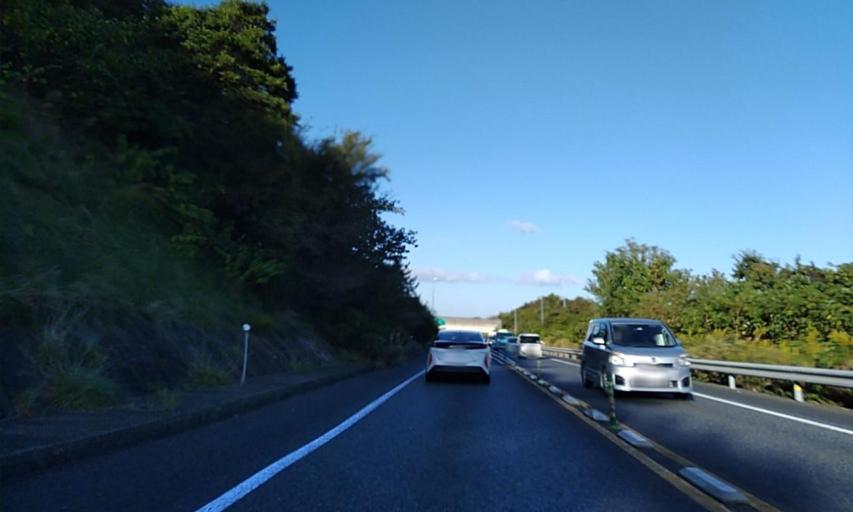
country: JP
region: Wakayama
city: Iwade
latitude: 34.3334
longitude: 135.2291
